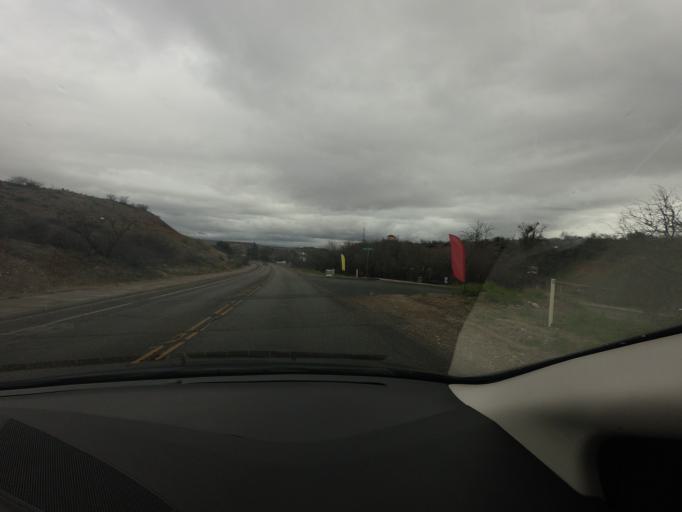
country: US
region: Arizona
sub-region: Yavapai County
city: Cottonwood
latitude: 34.7505
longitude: -112.0314
